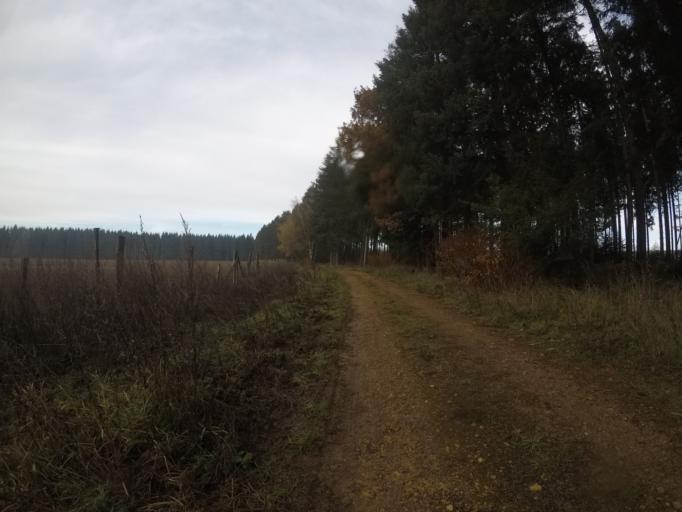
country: BE
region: Wallonia
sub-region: Province du Luxembourg
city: Habay-la-Vieille
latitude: 49.7362
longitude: 5.5985
